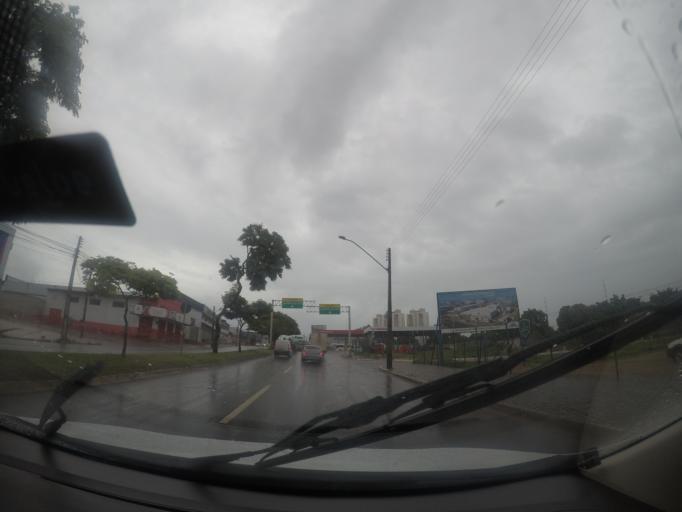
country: BR
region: Goias
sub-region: Goiania
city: Goiania
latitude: -16.6631
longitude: -49.3264
